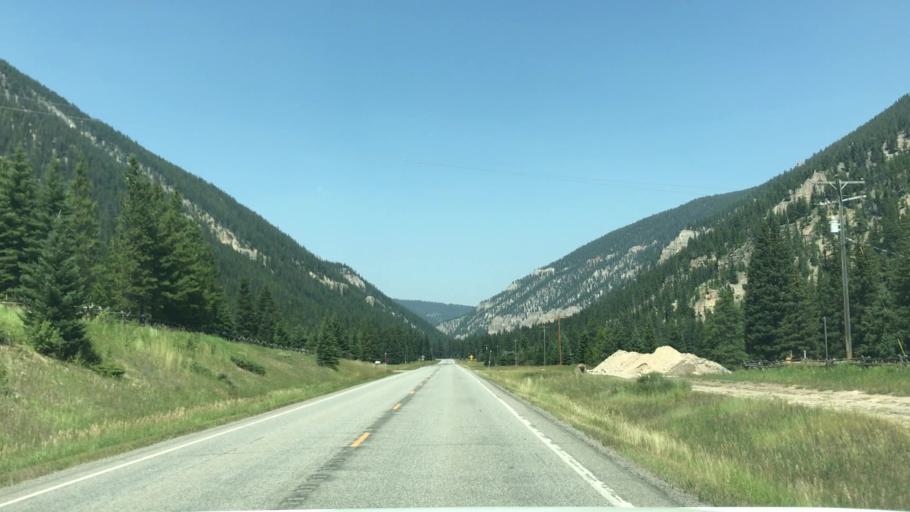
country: US
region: Montana
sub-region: Gallatin County
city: Big Sky
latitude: 45.1193
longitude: -111.2272
